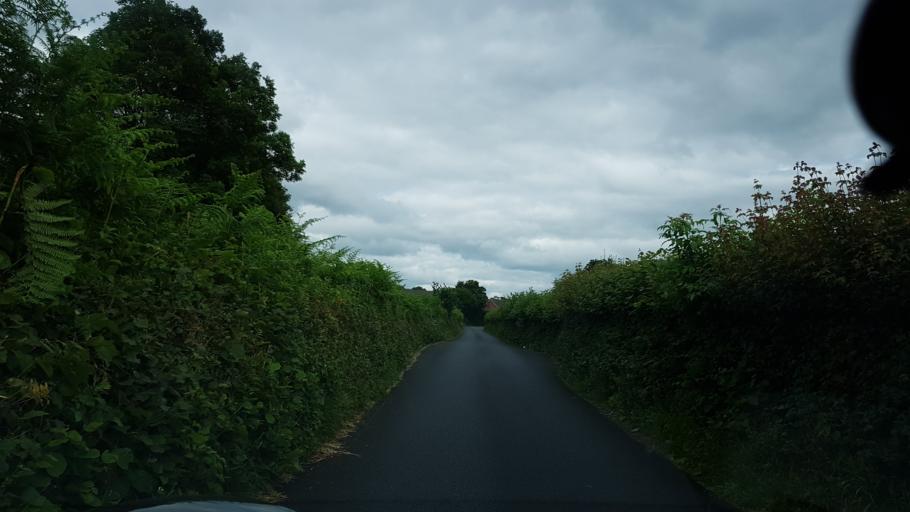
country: GB
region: Wales
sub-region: Monmouthshire
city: Gilwern
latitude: 51.8339
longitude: -3.0983
